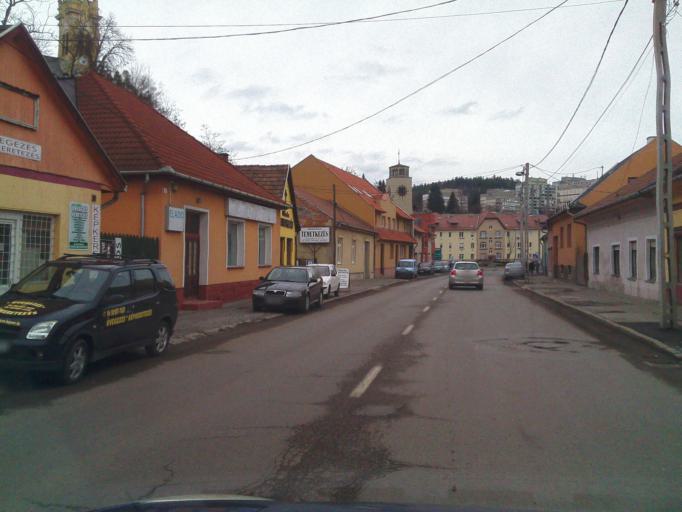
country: HU
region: Nograd
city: Salgotarjan
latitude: 48.1107
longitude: 19.8117
